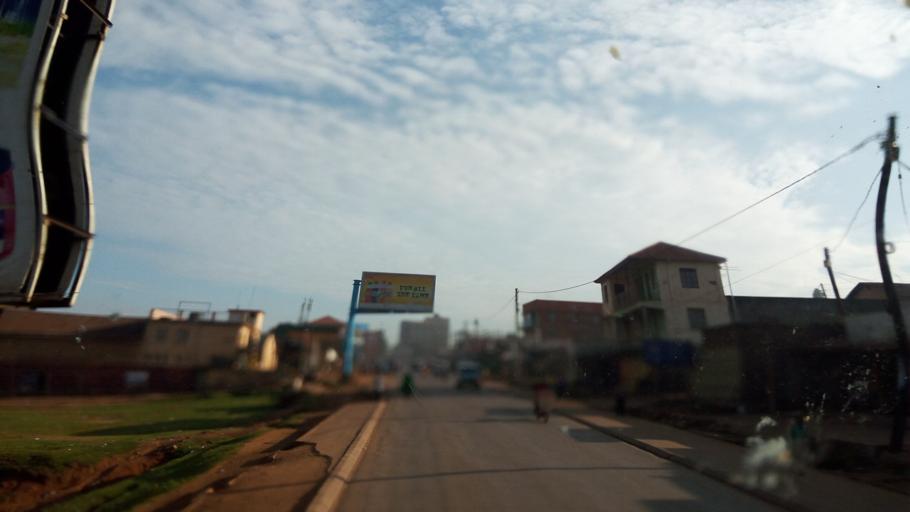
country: UG
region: Central Region
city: Kampala Central Division
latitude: 0.3570
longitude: 32.5624
